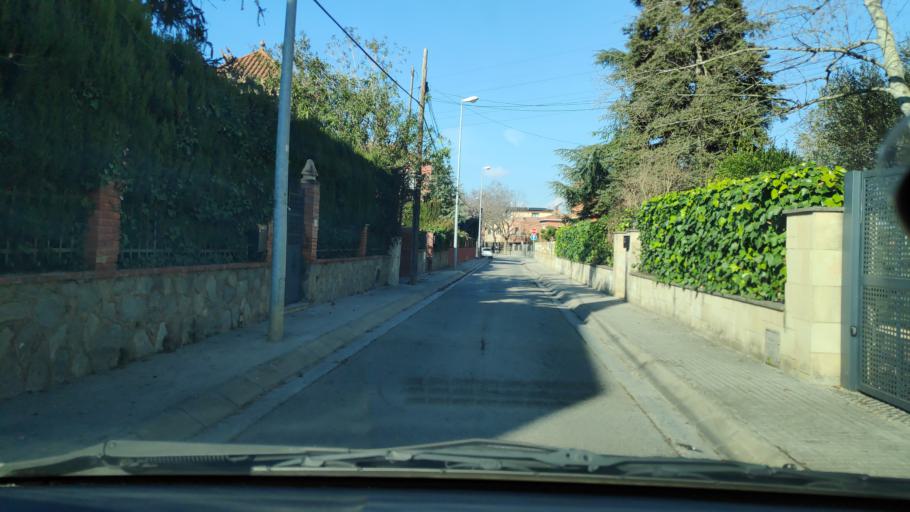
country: ES
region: Catalonia
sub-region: Provincia de Barcelona
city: Sant Cugat del Valles
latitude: 41.4557
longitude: 2.0701
